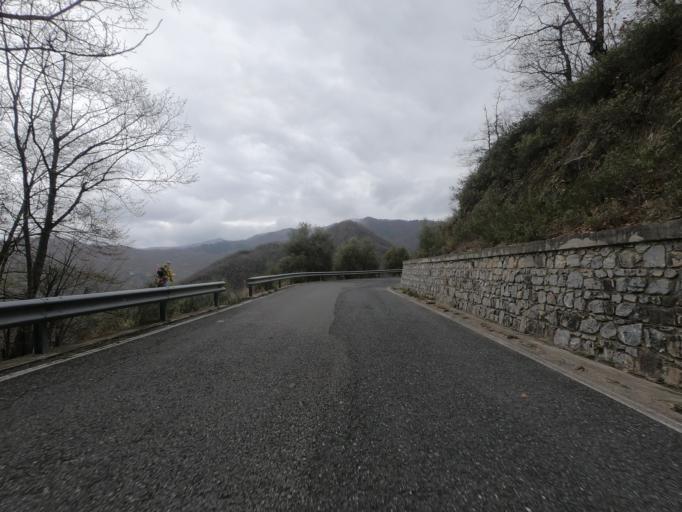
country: IT
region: Liguria
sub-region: Provincia di Savona
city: Testico
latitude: 44.0255
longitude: 8.0086
